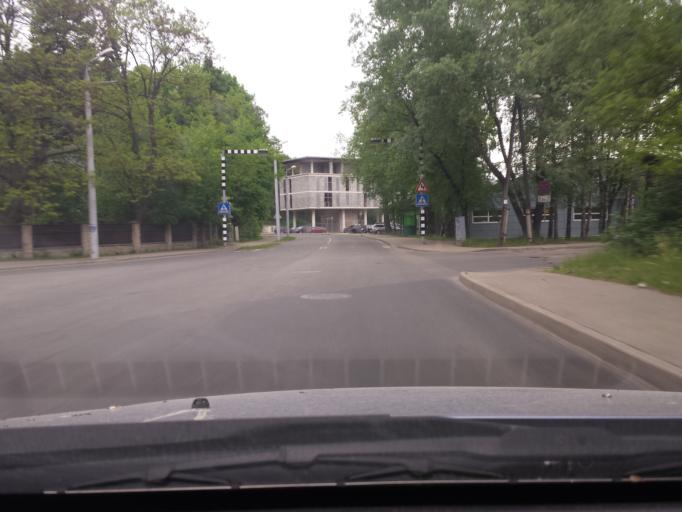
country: LV
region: Riga
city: Jaunciems
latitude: 57.0016
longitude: 24.1705
